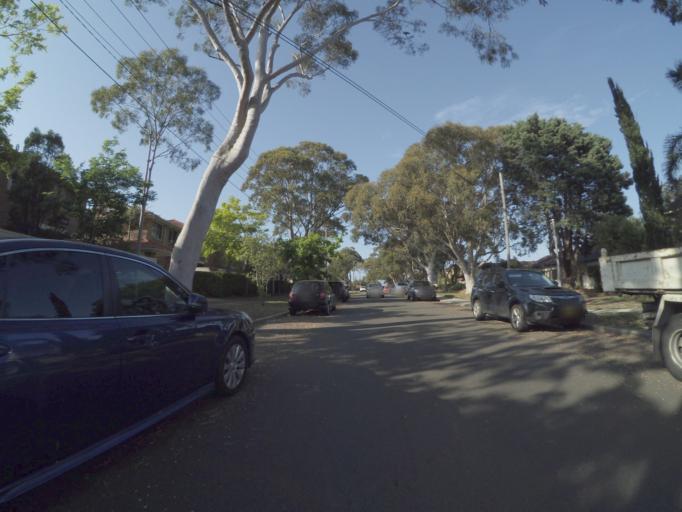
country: AU
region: New South Wales
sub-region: Sutherland Shire
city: Caringbah
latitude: -34.0446
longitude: 151.1174
